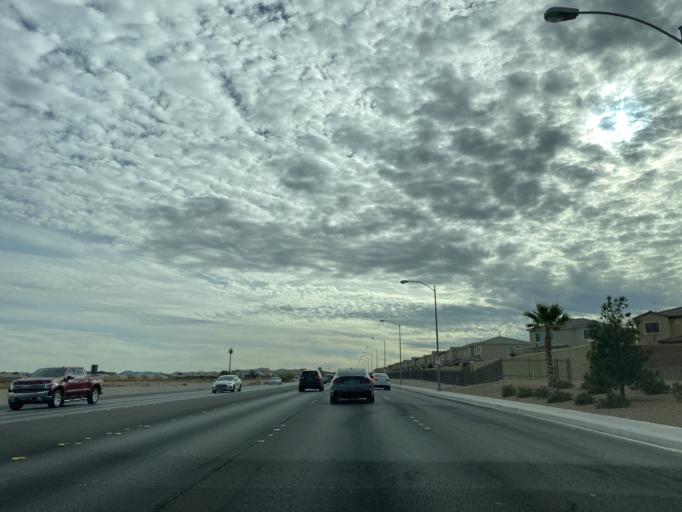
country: US
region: Nevada
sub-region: Clark County
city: Enterprise
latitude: 36.0468
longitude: -115.2792
